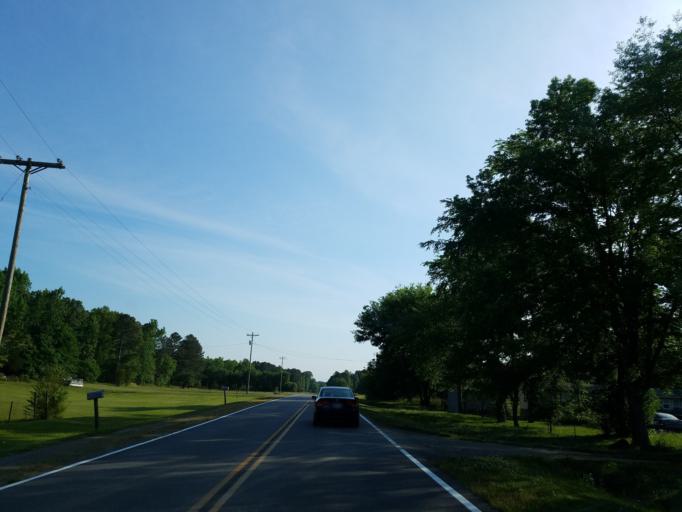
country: US
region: Georgia
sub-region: Chattooga County
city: Trion
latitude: 34.5498
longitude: -85.1981
